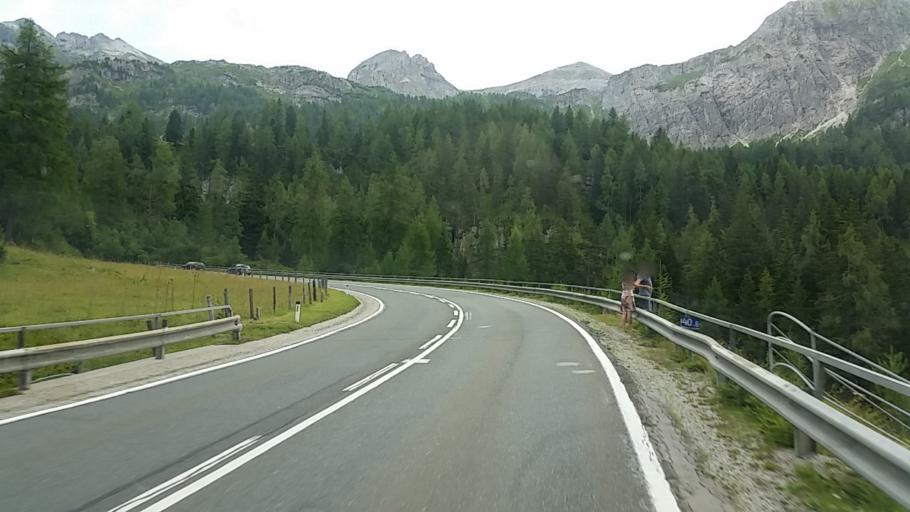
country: AT
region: Salzburg
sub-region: Politischer Bezirk Sankt Johann im Pongau
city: Untertauern
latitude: 47.2522
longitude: 13.5088
